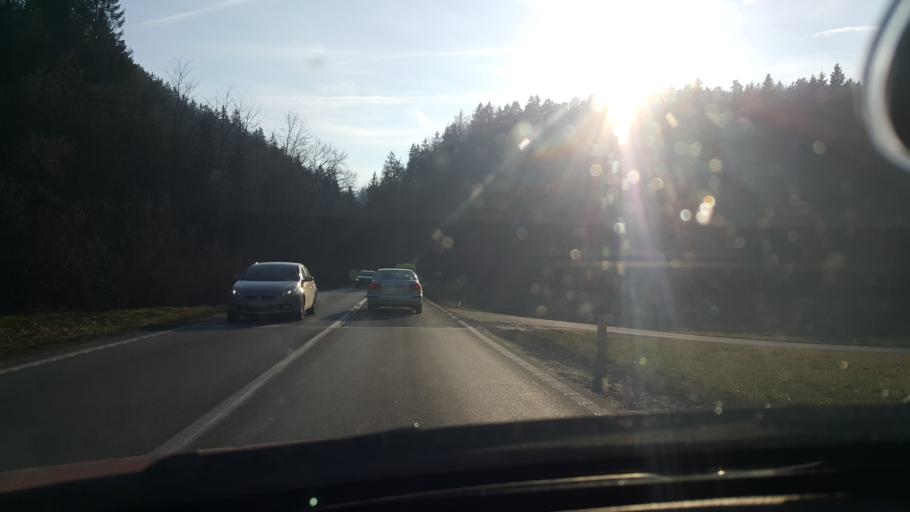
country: SI
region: Zalec
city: Gotovlje
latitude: 46.3177
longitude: 15.1764
